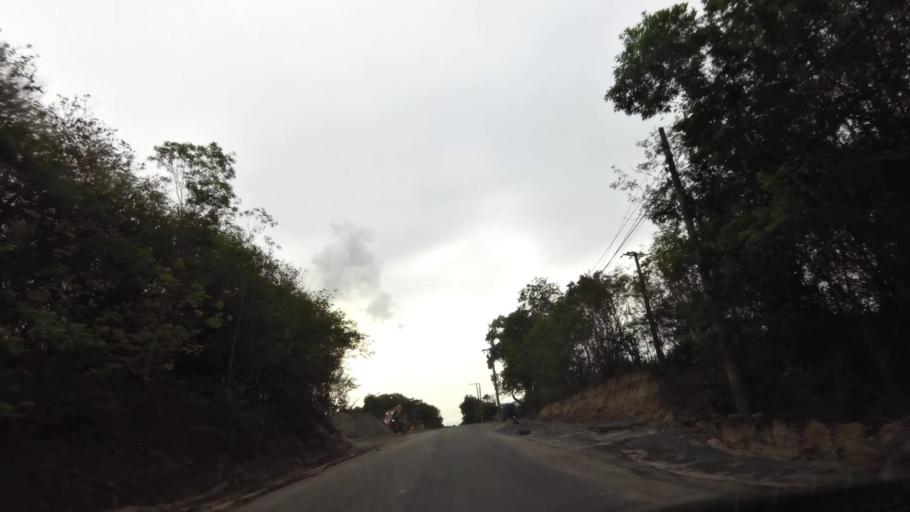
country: BR
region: Espirito Santo
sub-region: Piuma
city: Piuma
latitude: -20.7922
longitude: -40.5812
